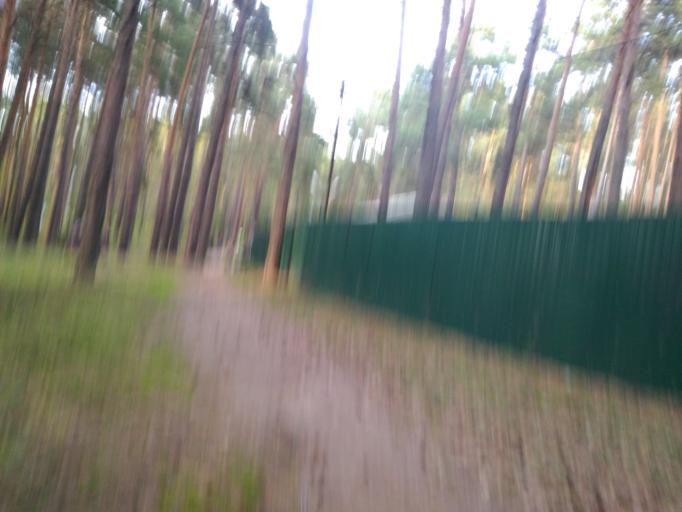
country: RU
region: Ulyanovsk
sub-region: Ulyanovskiy Rayon
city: Ulyanovsk
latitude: 54.3602
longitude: 48.5155
